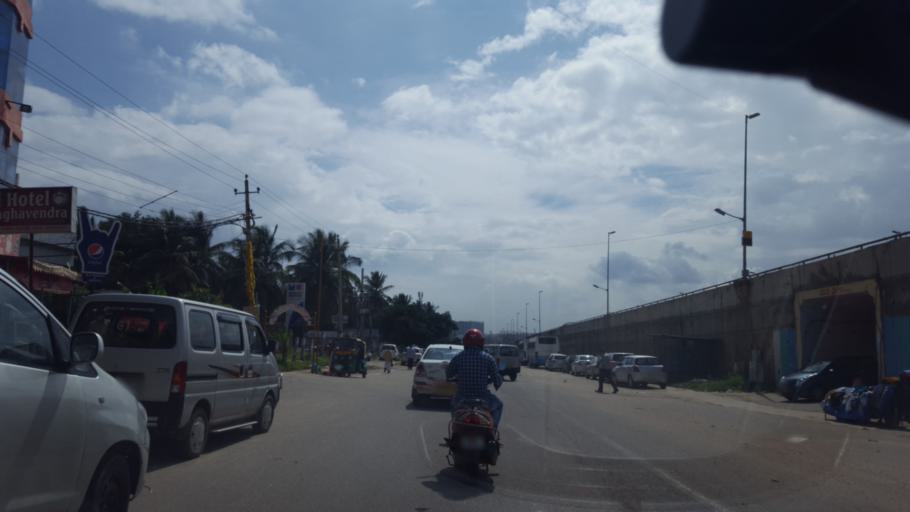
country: IN
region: Karnataka
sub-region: Bangalore Urban
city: Yelahanka
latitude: 13.1114
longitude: 77.6052
